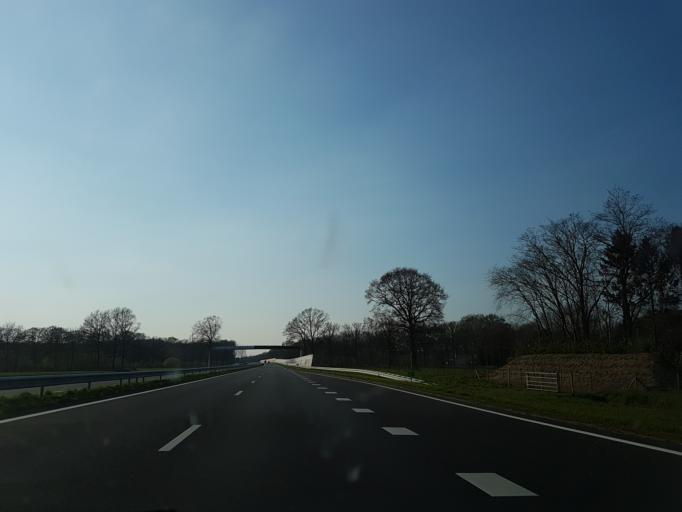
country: NL
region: Overijssel
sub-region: Gemeente Raalte
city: Heino
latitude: 52.4855
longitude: 6.1717
